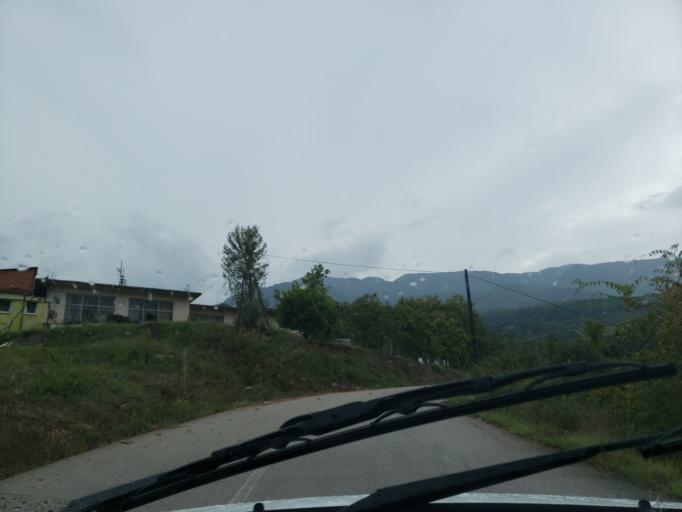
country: GR
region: Central Greece
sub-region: Nomos Fthiotidos
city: Anthili
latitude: 38.7953
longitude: 22.4839
